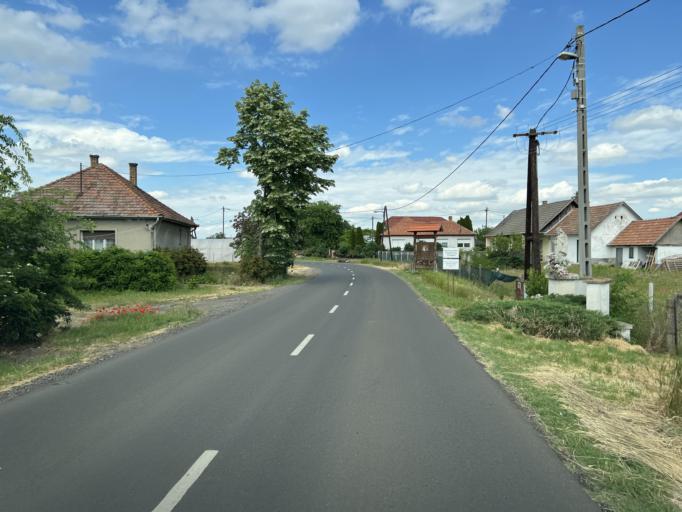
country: HU
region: Pest
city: Szentlorinckata
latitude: 47.5251
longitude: 19.7607
